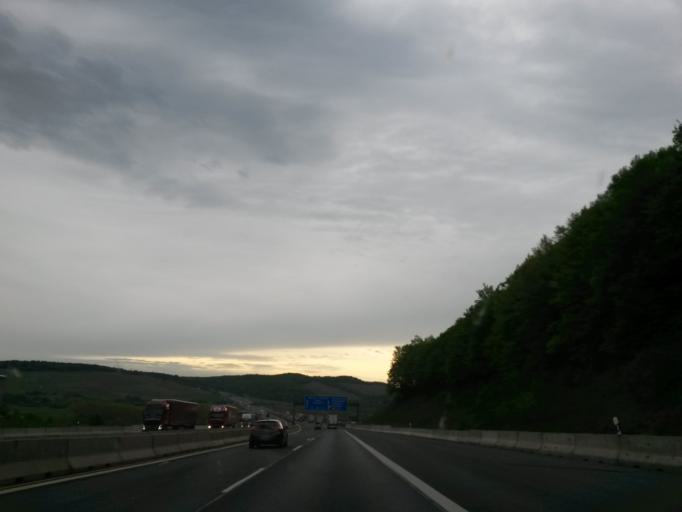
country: DE
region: Bavaria
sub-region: Regierungsbezirk Unterfranken
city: Randersacker
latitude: 49.7389
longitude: 9.9798
